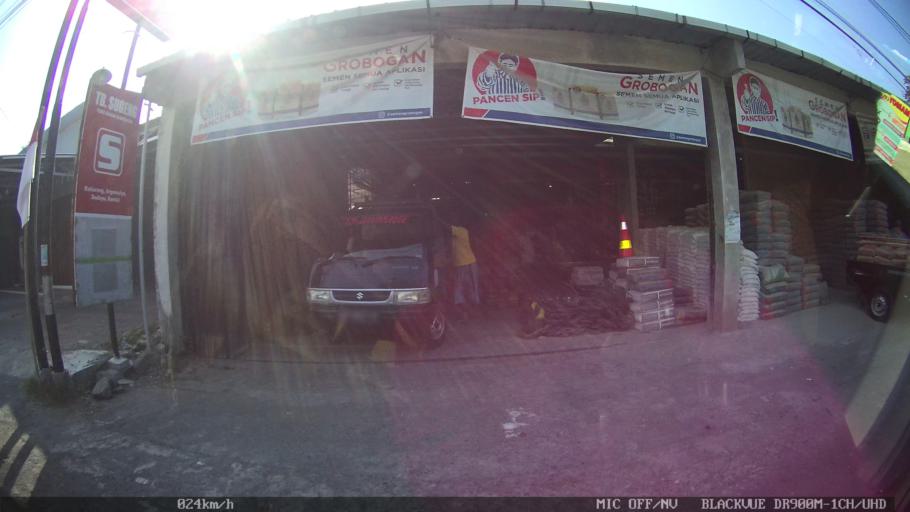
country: ID
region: Daerah Istimewa Yogyakarta
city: Kasihan
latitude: -7.8218
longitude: 110.2739
